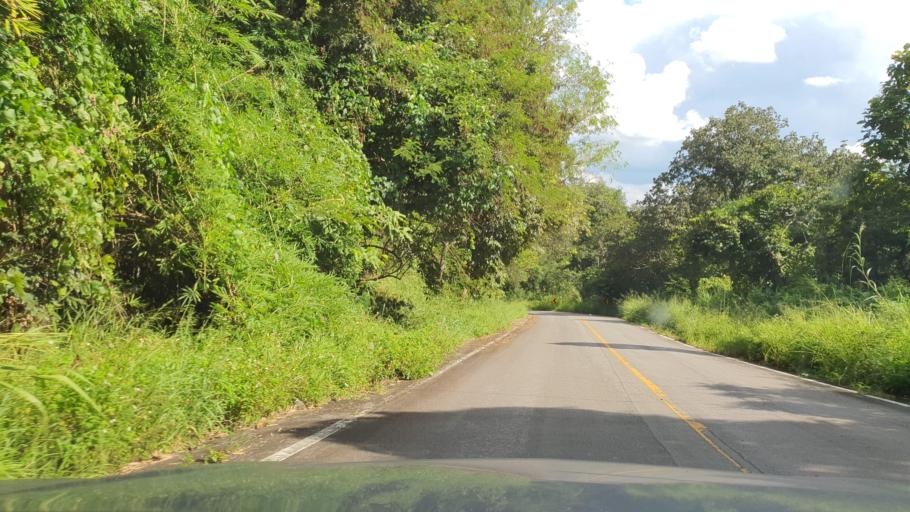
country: TH
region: Chiang Rai
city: Wiang Pa Pao
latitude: 19.3315
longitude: 99.4619
